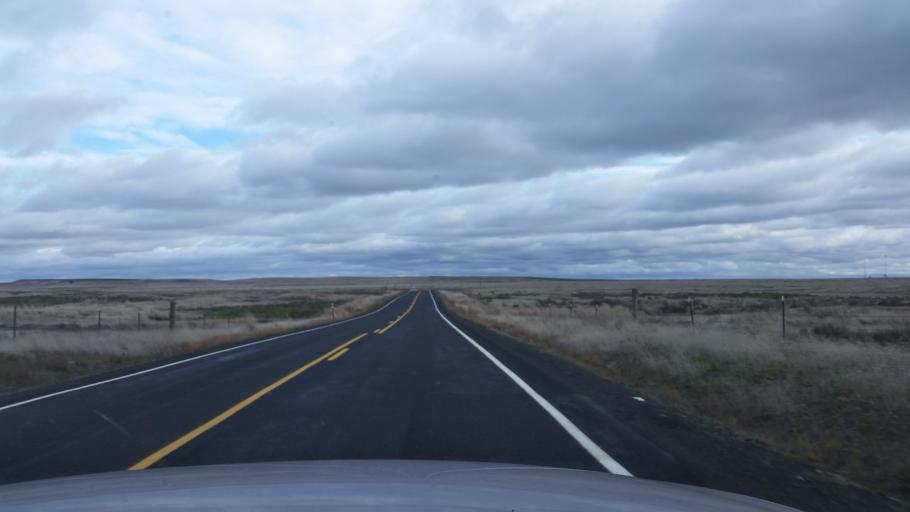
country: US
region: Washington
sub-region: Lincoln County
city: Davenport
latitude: 47.3339
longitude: -117.9900
